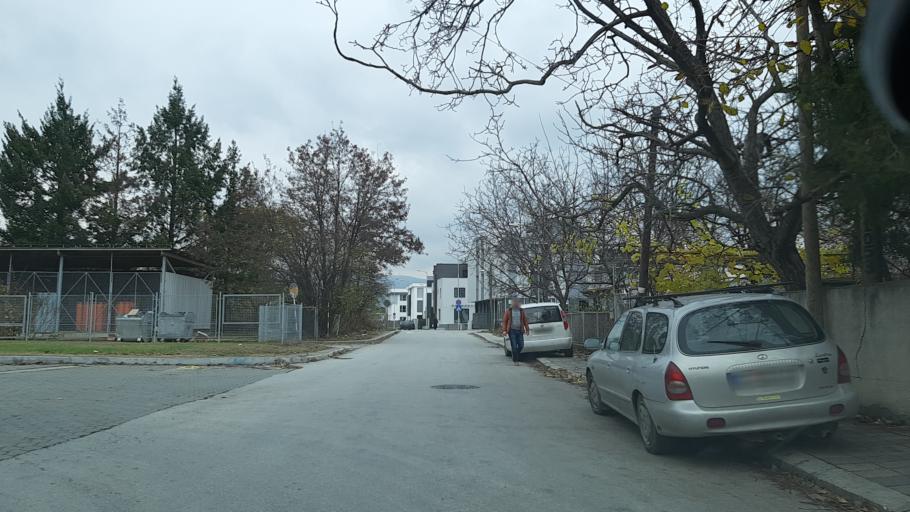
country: MK
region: Kisela Voda
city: Usje
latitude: 41.9784
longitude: 21.4674
